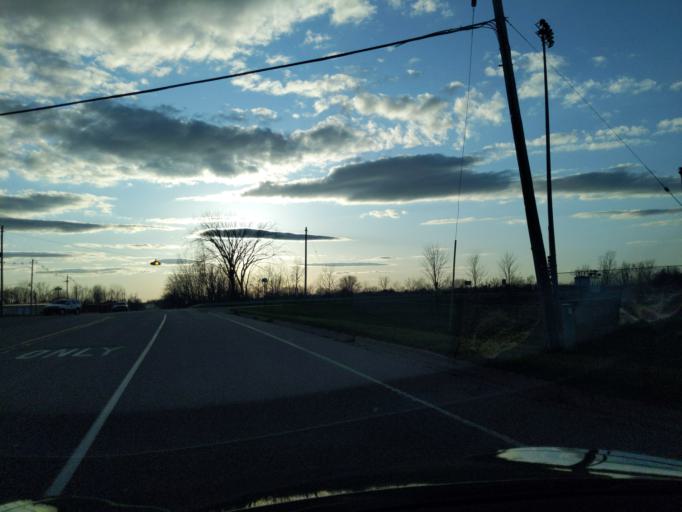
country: US
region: Michigan
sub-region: Ingham County
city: Mason
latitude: 42.5677
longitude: -84.4345
